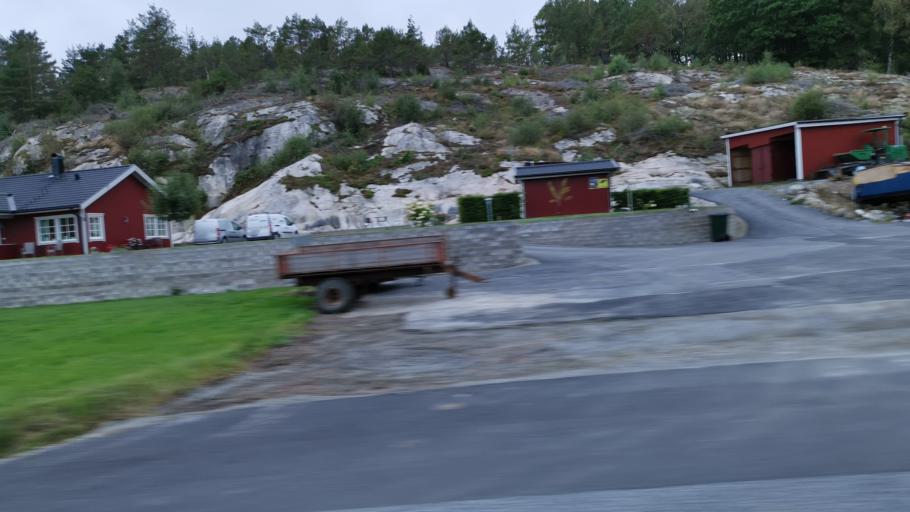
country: SE
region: Vaestra Goetaland
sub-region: Tanums Kommun
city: Tanumshede
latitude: 58.6285
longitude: 11.3494
